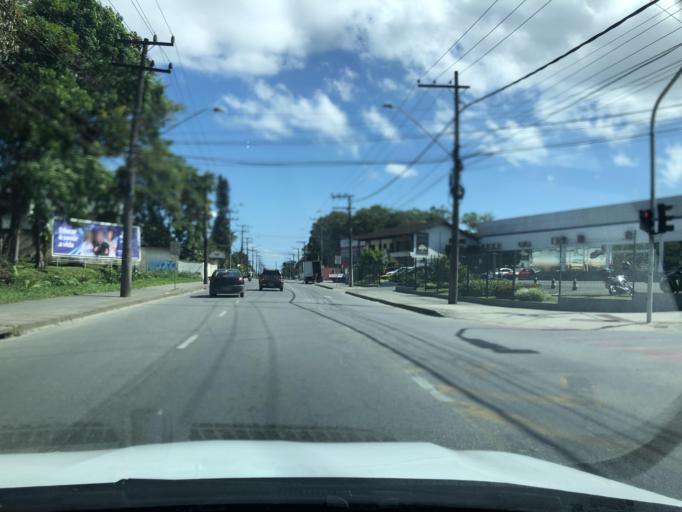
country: BR
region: Santa Catarina
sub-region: Joinville
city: Joinville
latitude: -26.2595
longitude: -48.8516
